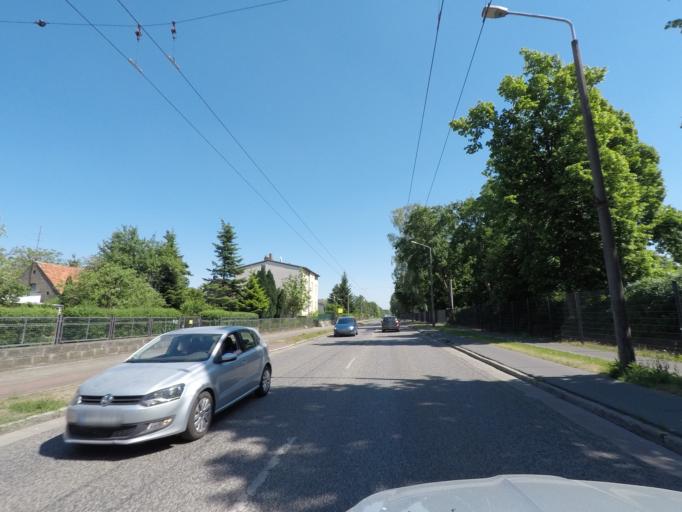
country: DE
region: Brandenburg
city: Melchow
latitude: 52.8383
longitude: 13.7400
